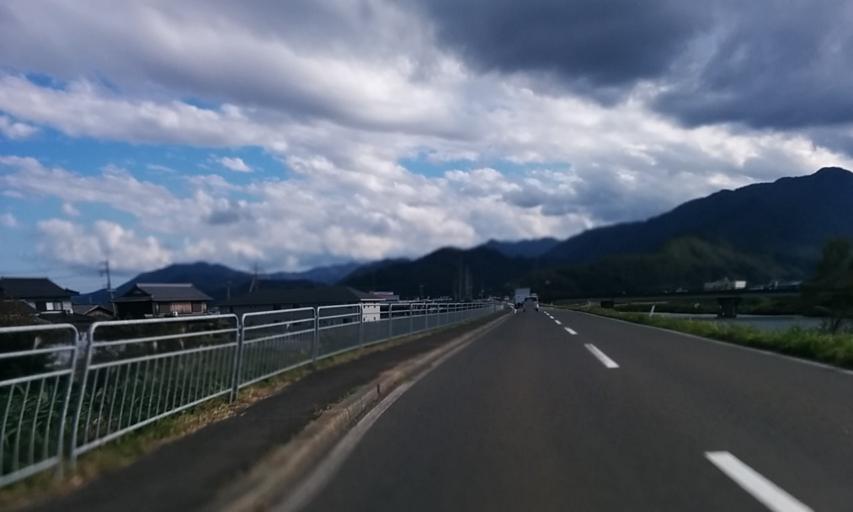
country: JP
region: Fukui
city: Obama
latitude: 35.4979
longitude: 135.7533
